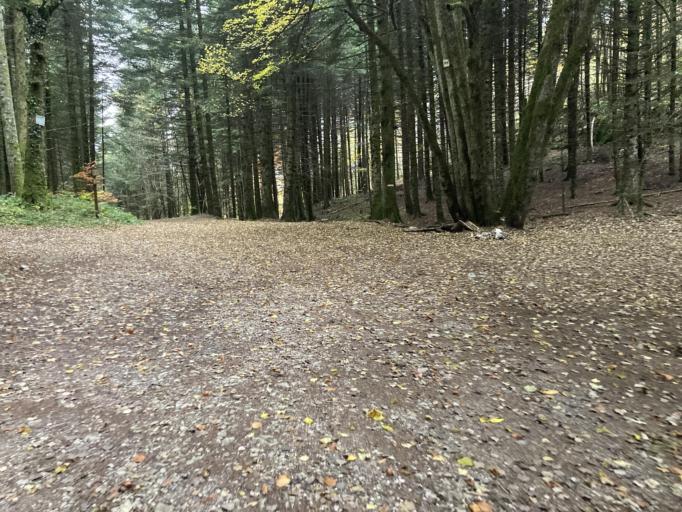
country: FR
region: Rhone-Alpes
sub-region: Departement de la Haute-Savoie
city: Veyrier-du-Lac
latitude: 45.9112
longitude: 6.1742
